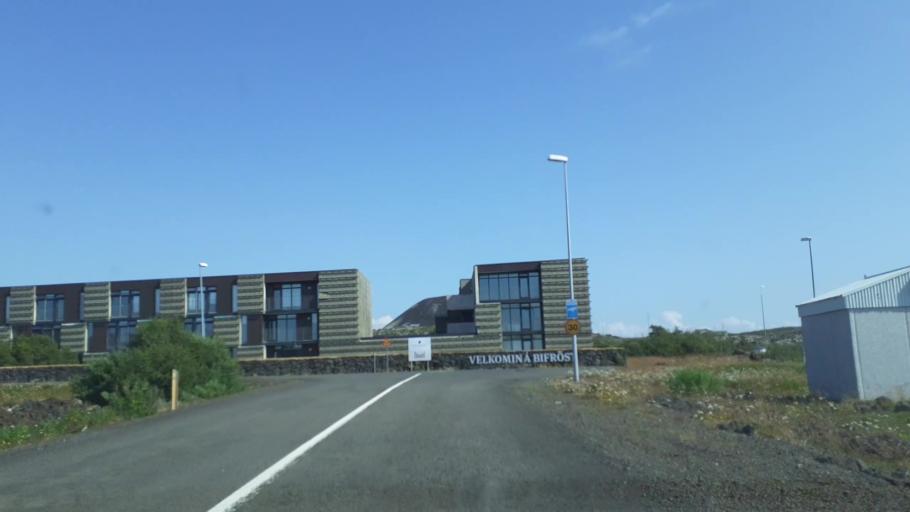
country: IS
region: West
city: Borgarnes
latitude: 64.7647
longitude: -21.5542
